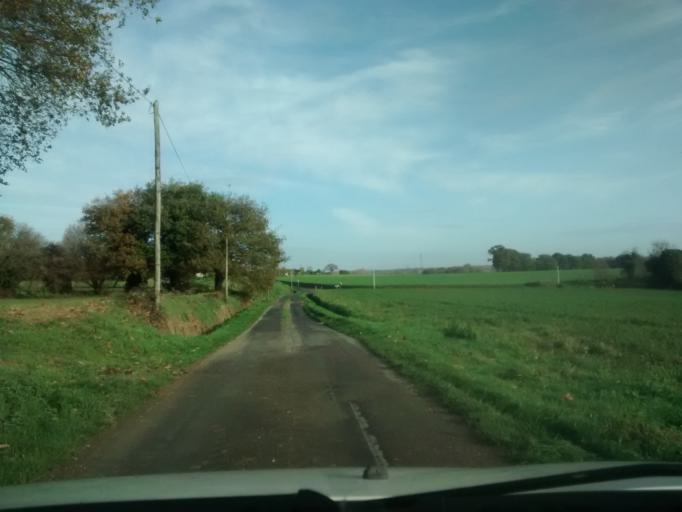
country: FR
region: Brittany
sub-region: Departement d'Ille-et-Vilaine
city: Brece
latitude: 48.1292
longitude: -1.4912
